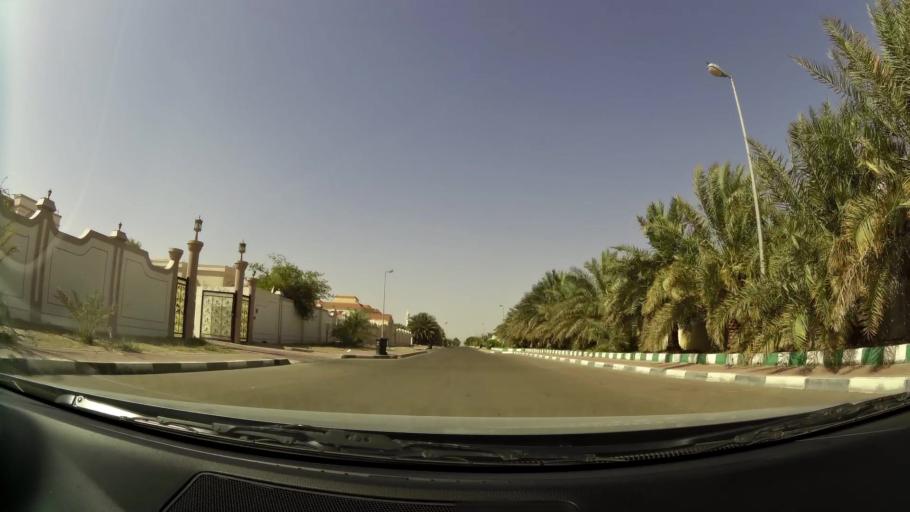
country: OM
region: Al Buraimi
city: Al Buraymi
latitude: 24.3138
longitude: 55.8076
